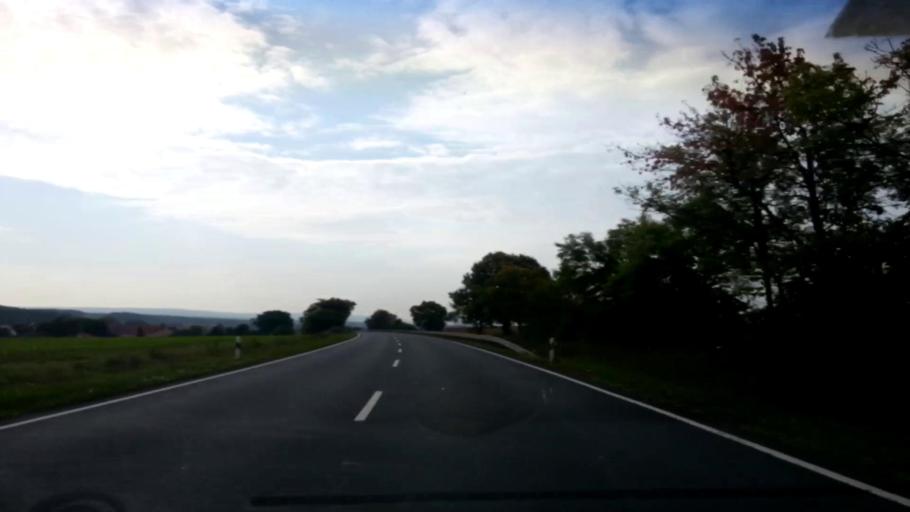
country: DE
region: Bavaria
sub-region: Regierungsbezirk Unterfranken
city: Lulsfeld
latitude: 49.8592
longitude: 10.3501
